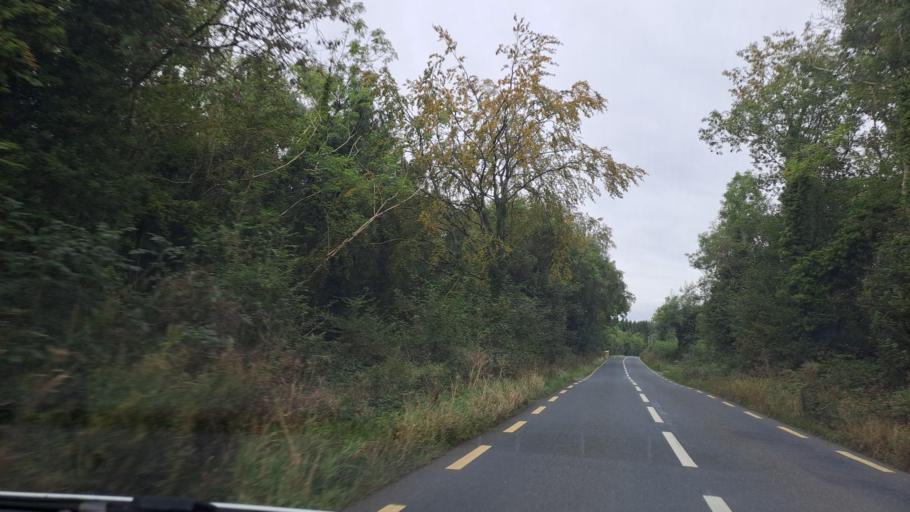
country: IE
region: Ulster
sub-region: An Cabhan
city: Kingscourt
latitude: 53.8952
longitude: -6.7621
